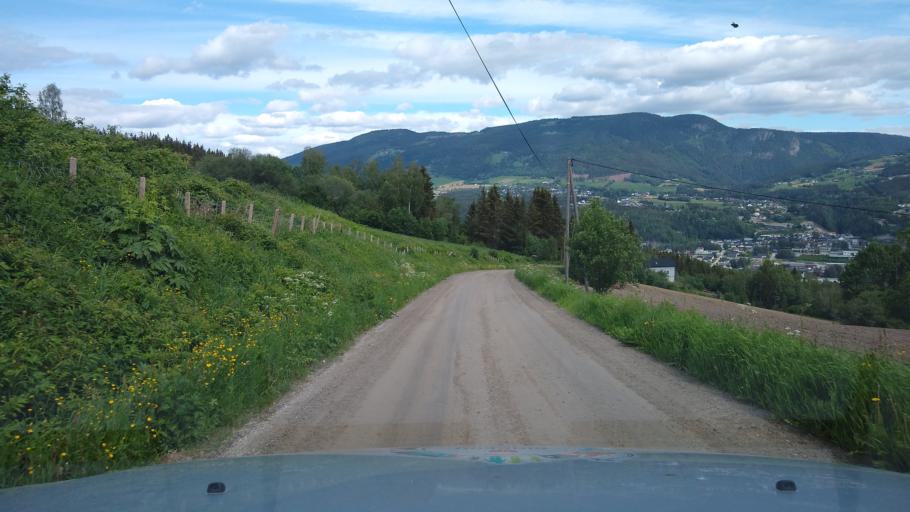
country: NO
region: Oppland
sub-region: Ringebu
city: Ringebu
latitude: 61.5145
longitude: 10.1330
